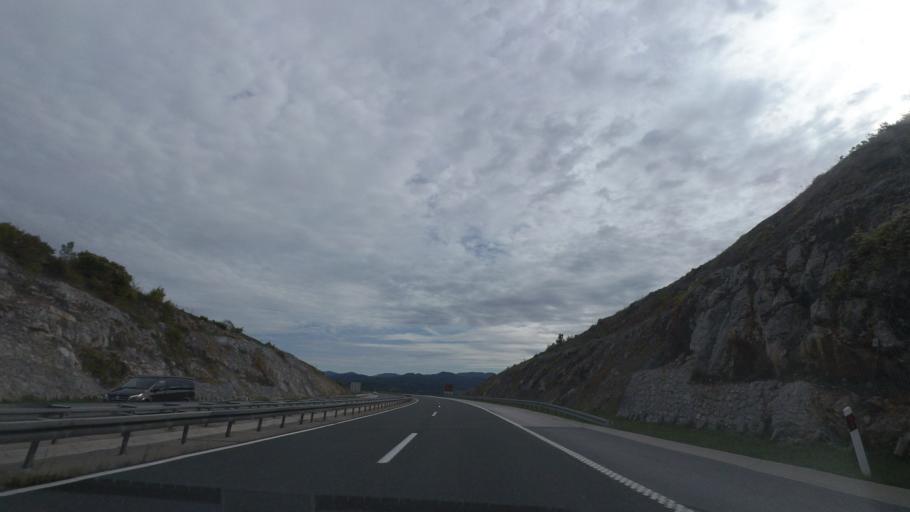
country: HR
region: Licko-Senjska
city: Otocac
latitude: 44.9154
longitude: 15.1702
